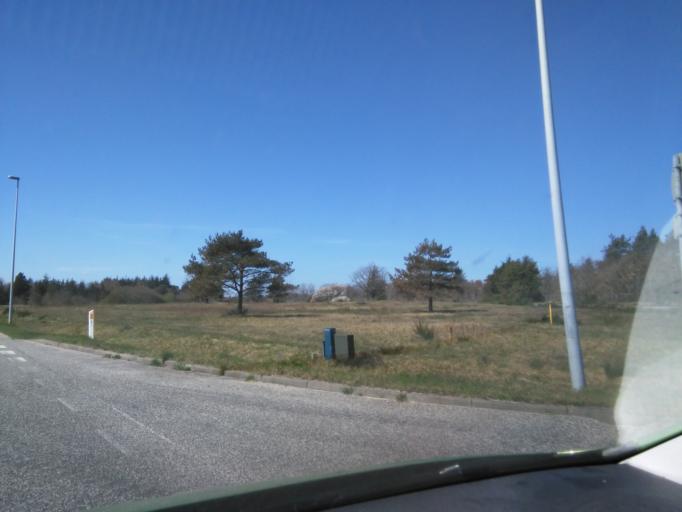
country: DK
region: South Denmark
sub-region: Varde Kommune
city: Oksbol
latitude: 55.6154
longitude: 8.2431
